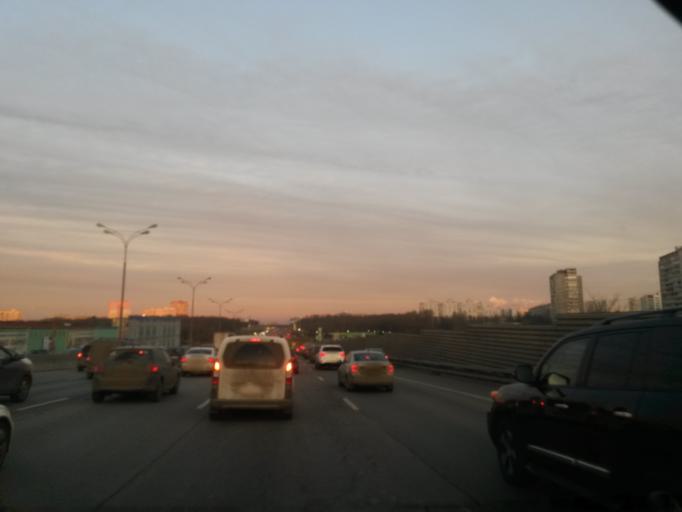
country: RU
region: Moscow
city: Tyoply Stan
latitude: 55.6154
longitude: 37.4873
